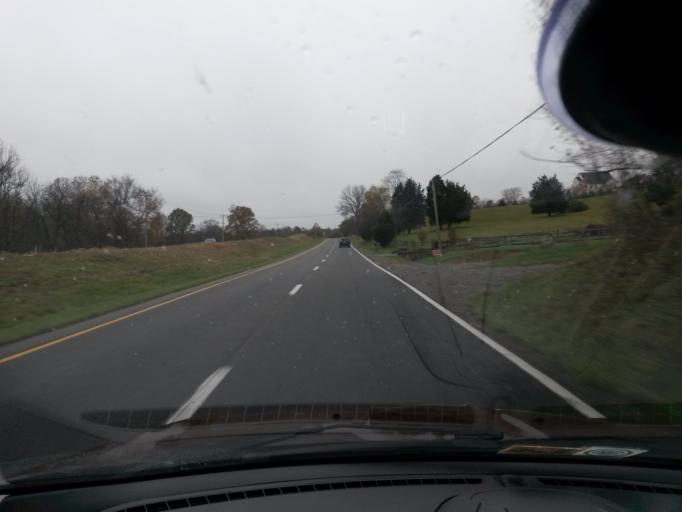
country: US
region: Virginia
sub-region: Botetourt County
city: Daleville
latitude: 37.4394
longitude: -79.9037
